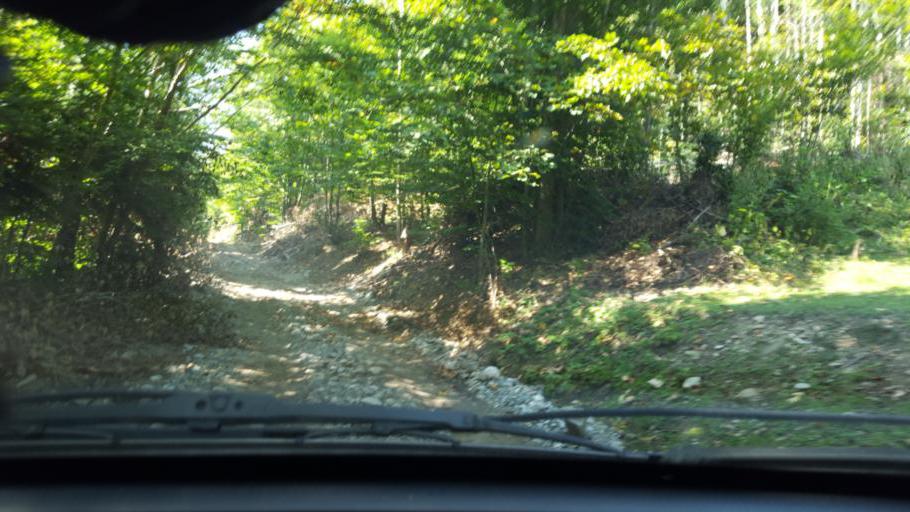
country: ME
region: Andrijevica
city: Andrijevica
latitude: 42.5860
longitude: 19.6328
